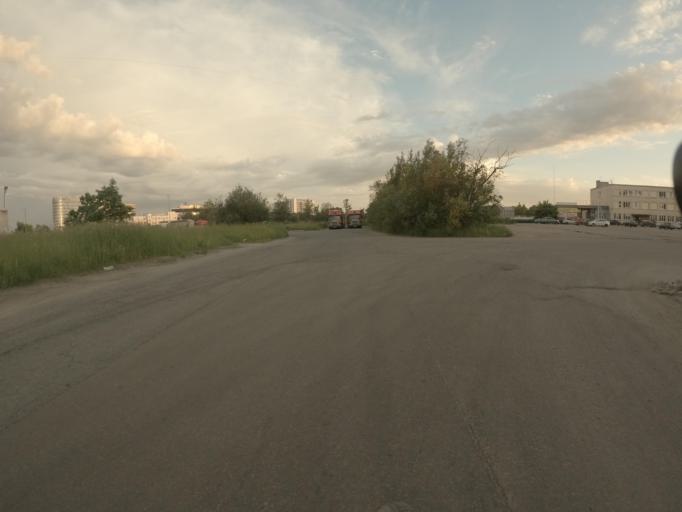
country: RU
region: St.-Petersburg
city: Kupchino
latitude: 59.8119
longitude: 30.3137
